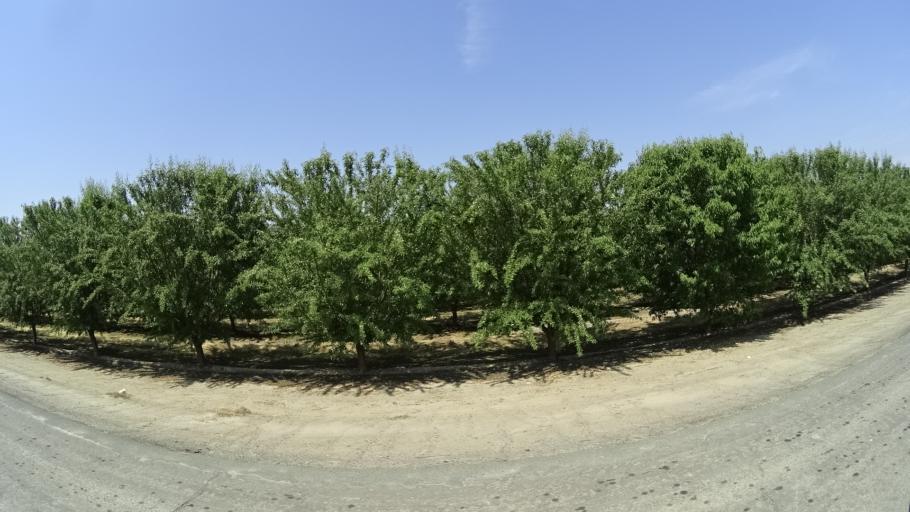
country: US
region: California
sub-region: Kings County
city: Lemoore
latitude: 36.3508
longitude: -119.7628
